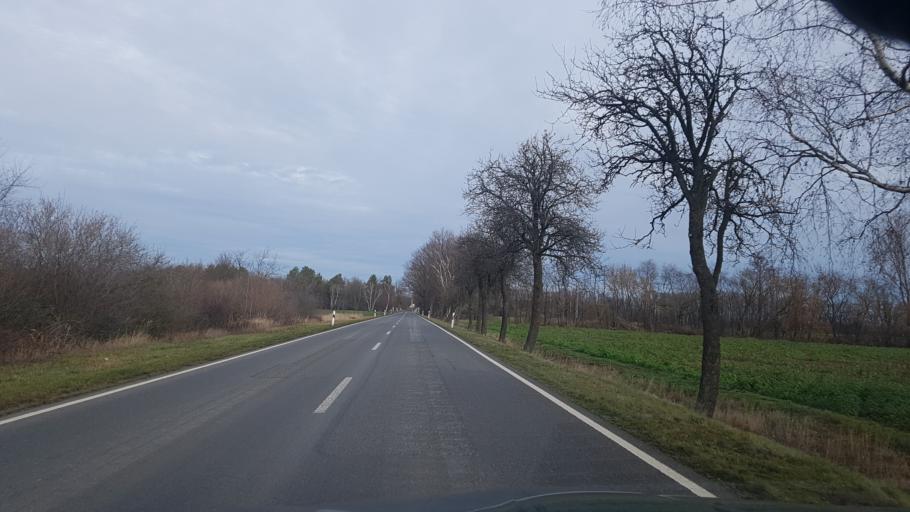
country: DE
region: Brandenburg
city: Bad Liebenwerda
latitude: 51.5322
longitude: 13.3423
